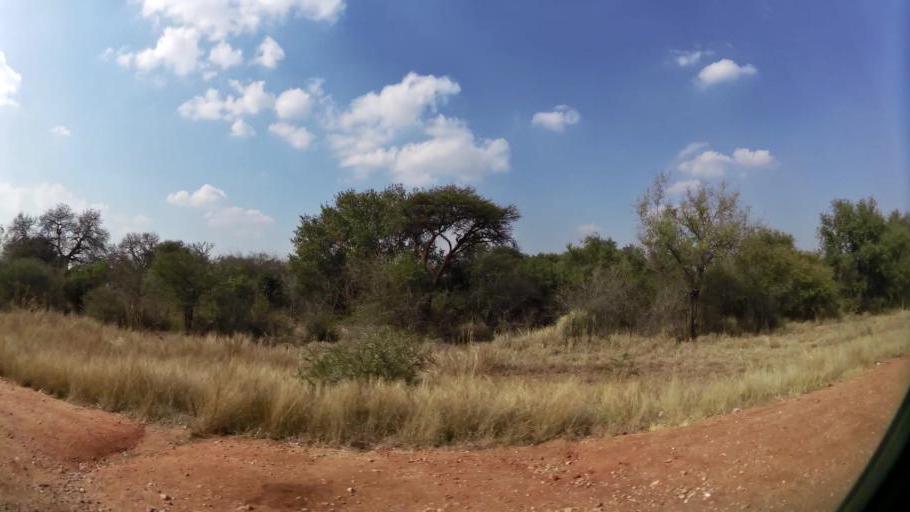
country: ZA
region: North-West
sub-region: Bojanala Platinum District Municipality
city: Mogwase
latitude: -25.4710
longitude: 27.0872
